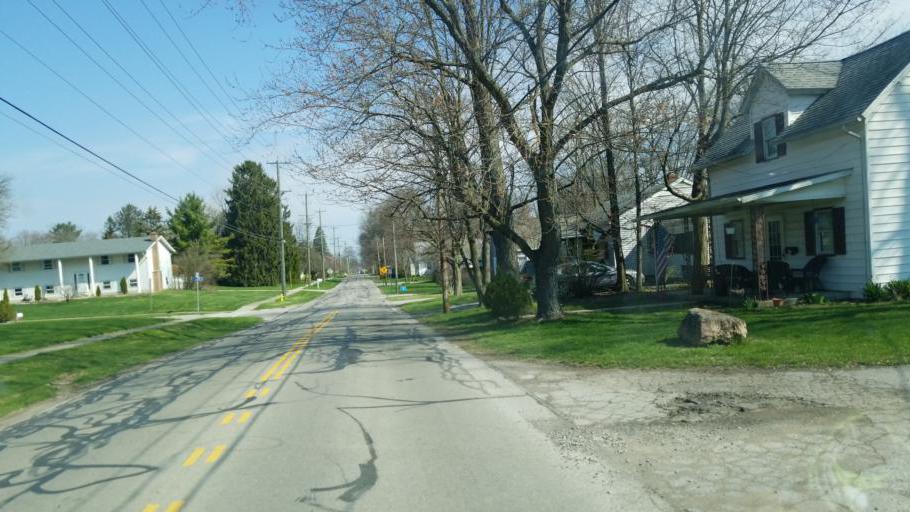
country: US
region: Ohio
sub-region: Delaware County
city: Delaware
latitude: 40.3030
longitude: -83.0789
